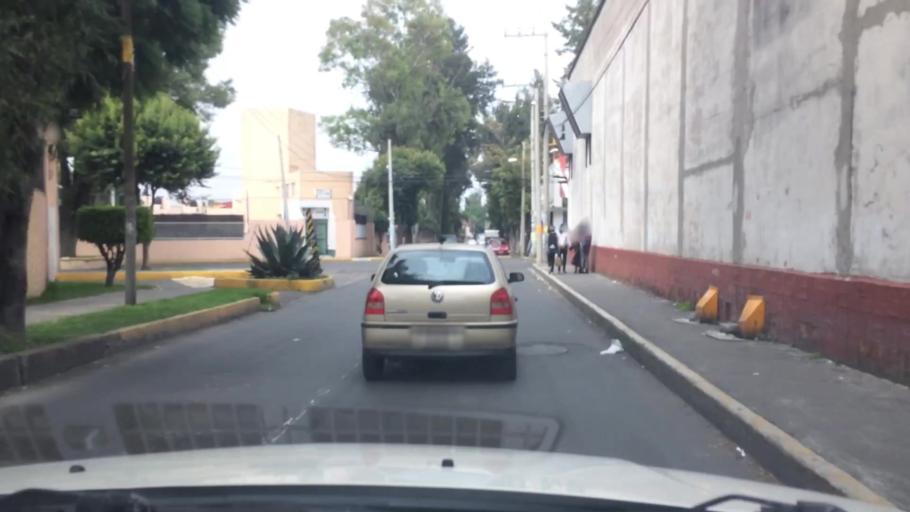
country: MX
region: Mexico City
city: Xochimilco
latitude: 19.2715
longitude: -99.1260
